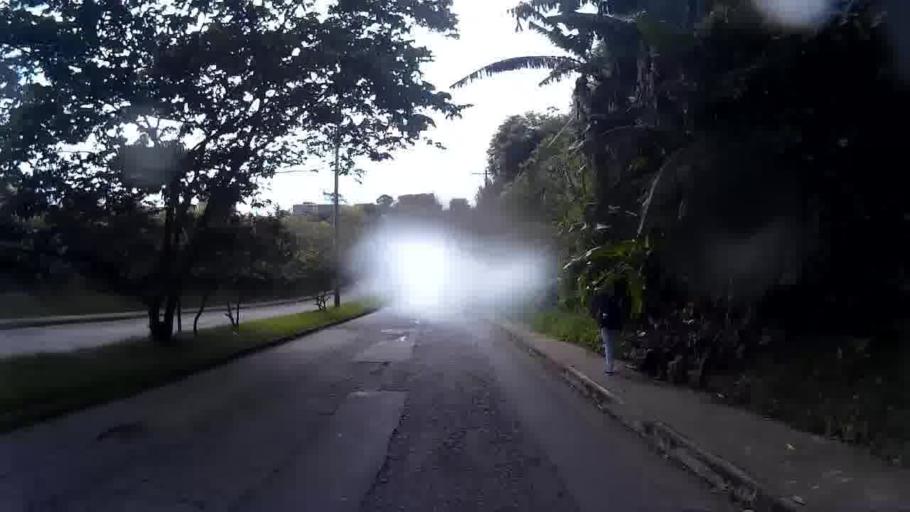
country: CO
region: Quindio
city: Calarca
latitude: 4.5597
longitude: -75.6485
